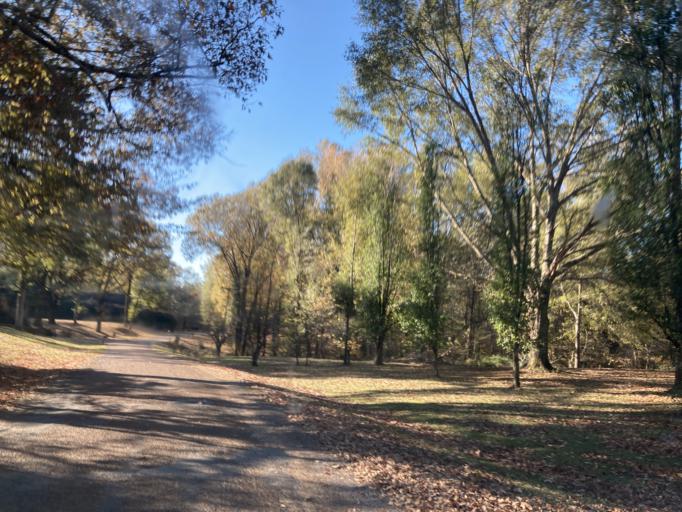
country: US
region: Mississippi
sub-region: Yazoo County
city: Yazoo City
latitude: 32.7952
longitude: -90.3559
